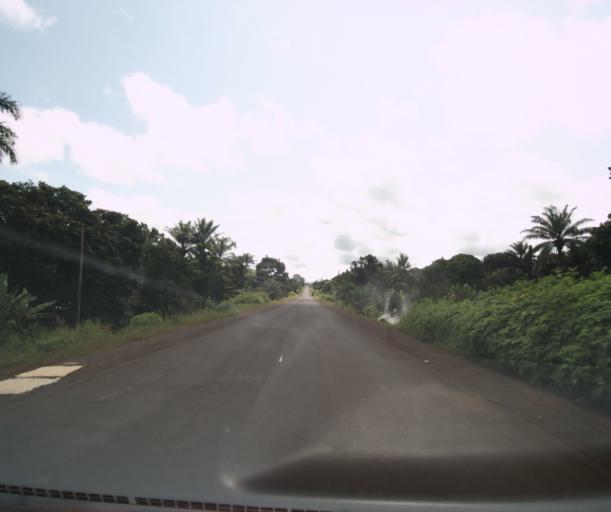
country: CM
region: West
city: Foumban
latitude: 5.6670
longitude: 10.7842
